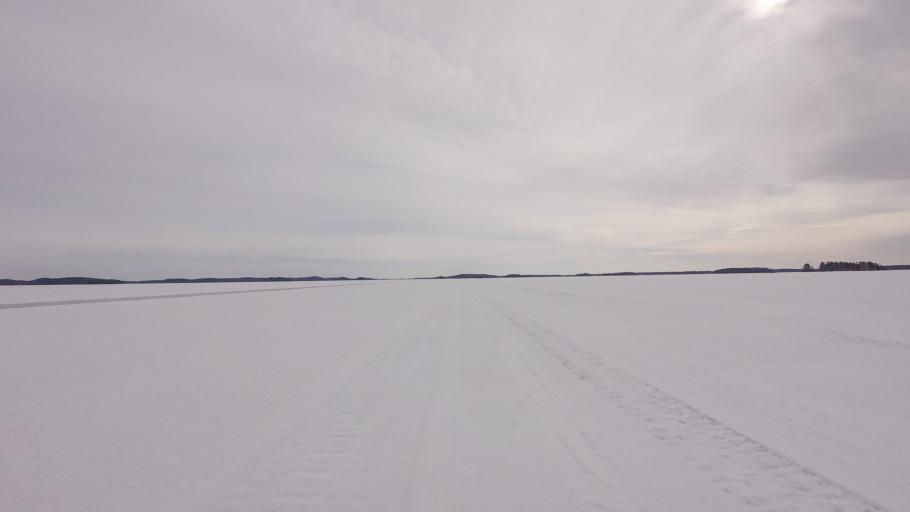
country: FI
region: Southern Savonia
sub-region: Savonlinna
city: Rantasalmi
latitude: 62.1121
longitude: 28.3832
